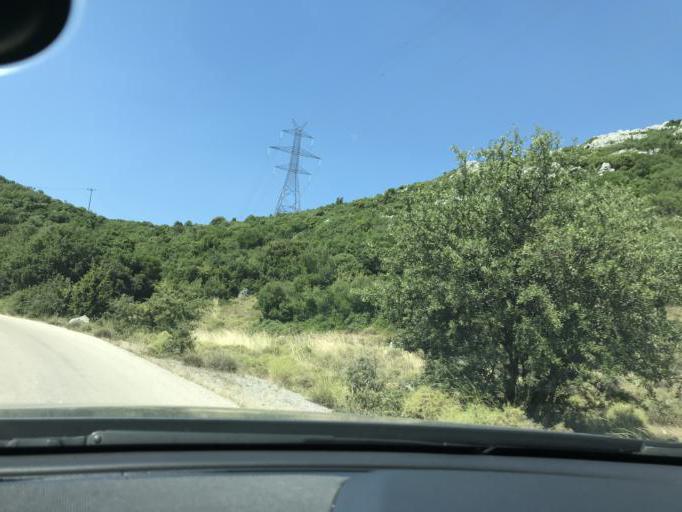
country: GR
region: Central Greece
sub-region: Nomos Voiotias
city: Distomo
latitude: 38.4957
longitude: 22.6973
